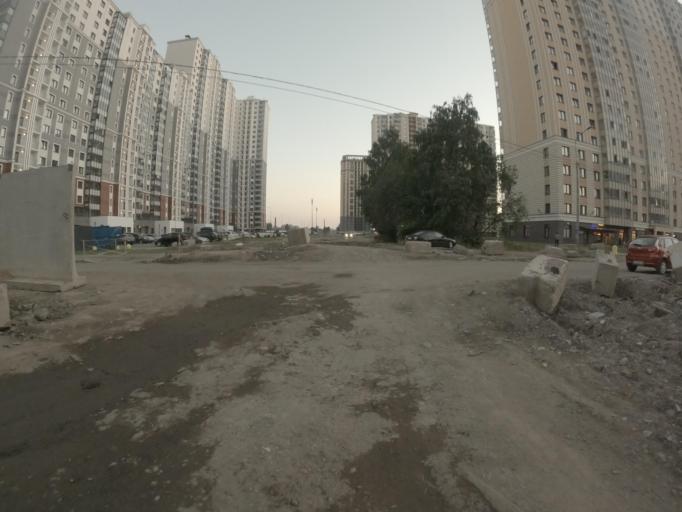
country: RU
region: St.-Petersburg
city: Obukhovo
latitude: 59.8997
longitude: 30.4524
